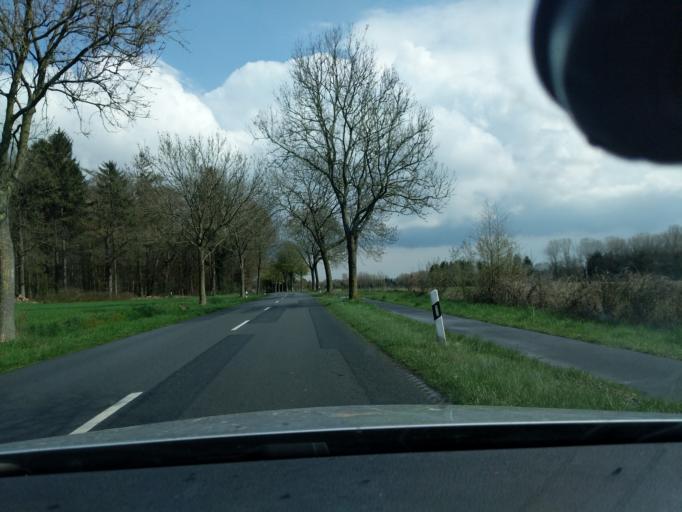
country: DE
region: Lower Saxony
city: Harsefeld
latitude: 53.4623
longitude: 9.4914
